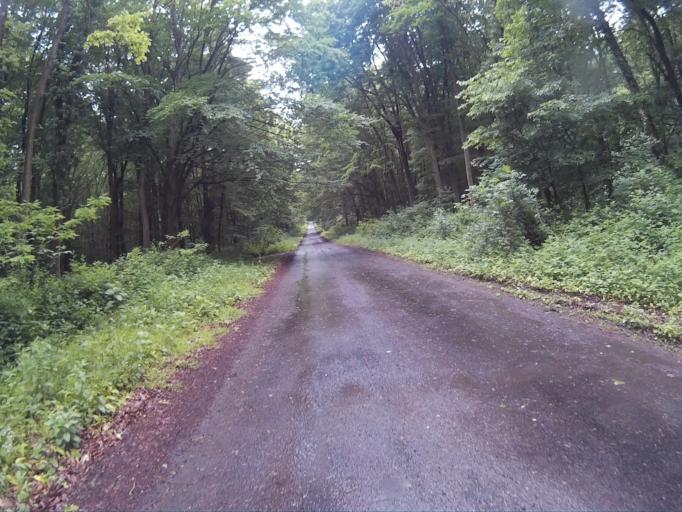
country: HU
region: Veszprem
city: Sumeg
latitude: 46.9388
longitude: 17.2907
